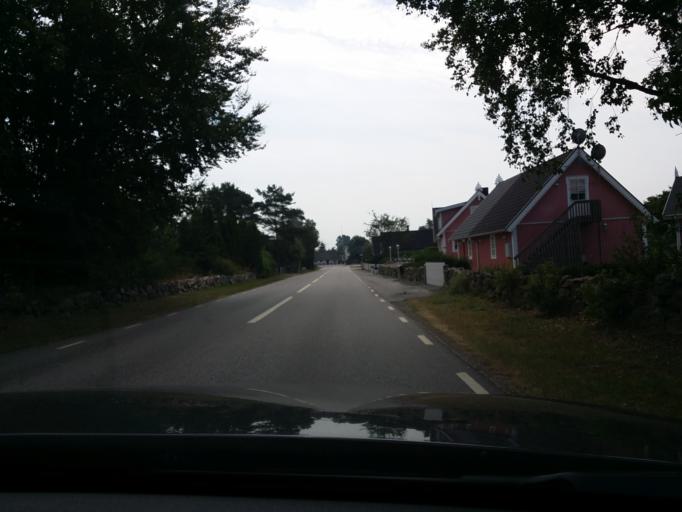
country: SE
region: Blekinge
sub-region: Solvesborgs Kommun
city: Soelvesborg
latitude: 56.0175
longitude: 14.7174
